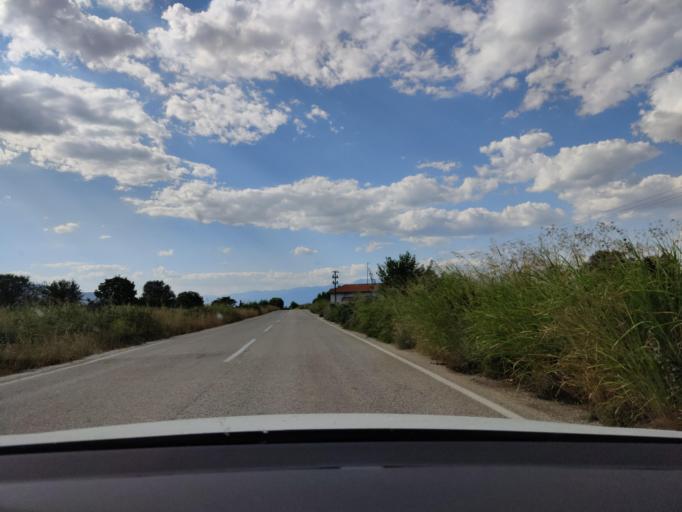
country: GR
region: Central Macedonia
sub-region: Nomos Serron
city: Strymoniko
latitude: 41.0767
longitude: 23.2956
